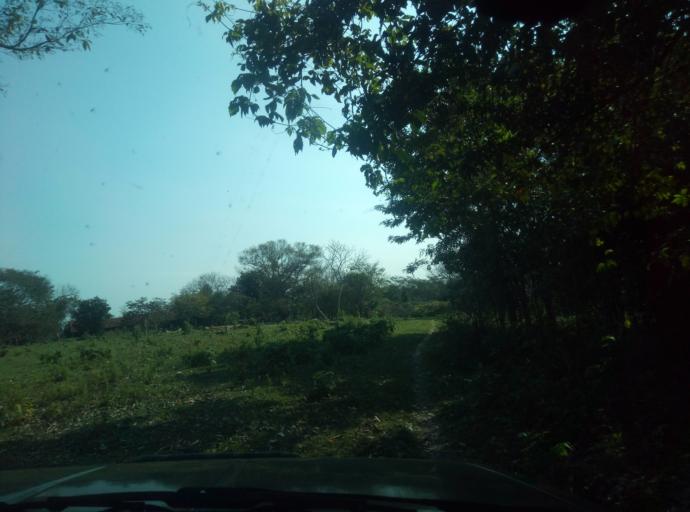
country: PY
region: Caaguazu
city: San Joaquin
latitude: -25.1581
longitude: -56.1302
